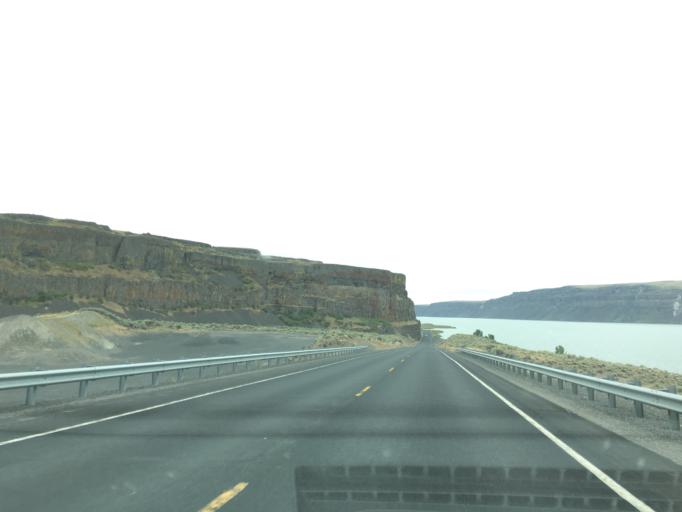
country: US
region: Washington
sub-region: Okanogan County
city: Coulee Dam
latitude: 47.7235
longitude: -119.2536
